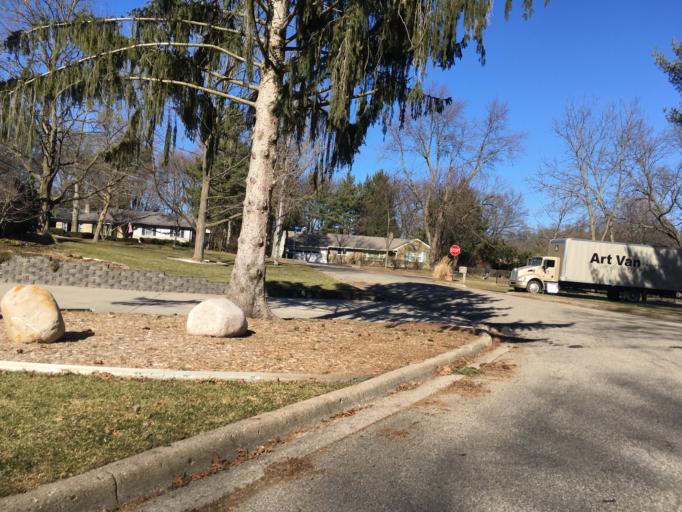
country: US
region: Michigan
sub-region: Kalamazoo County
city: Westwood
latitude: 42.2666
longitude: -85.6271
